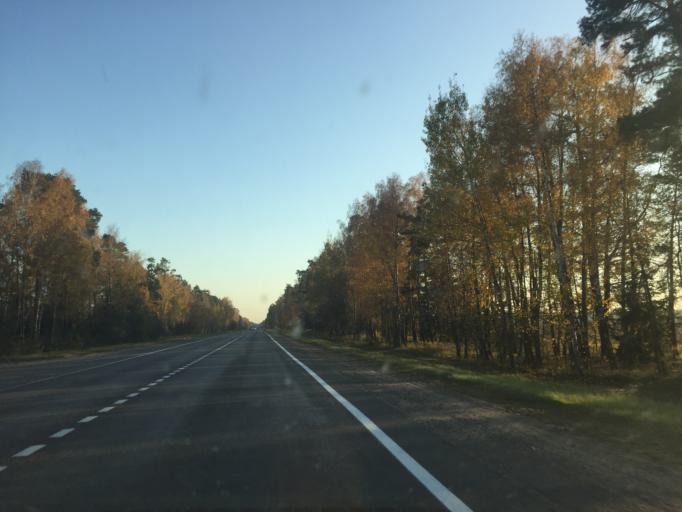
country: BY
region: Mogilev
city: Poselok Voskhod
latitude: 53.7279
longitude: 30.3669
